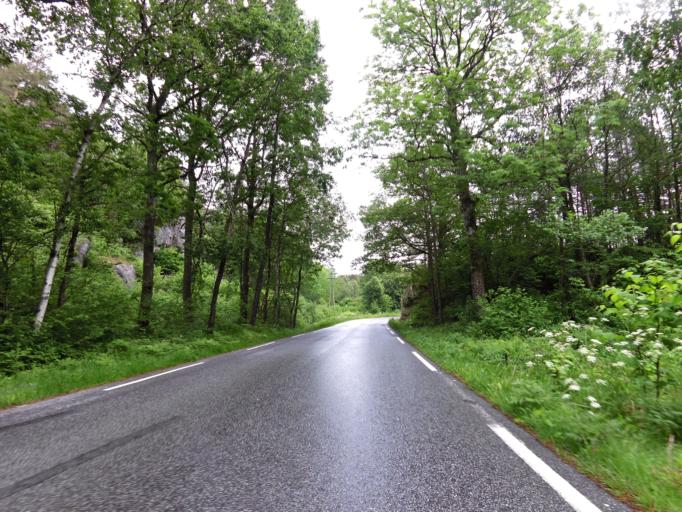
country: NO
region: Vest-Agder
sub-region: Mandal
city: Mandal
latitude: 58.0146
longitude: 7.5123
